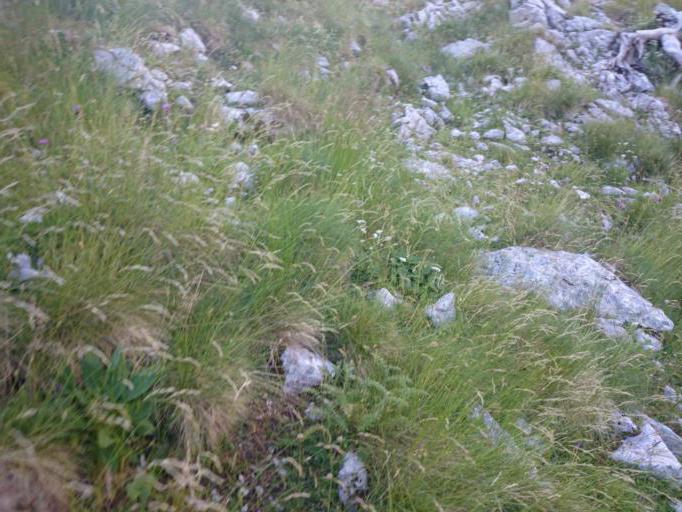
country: AL
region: Elbasan
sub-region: Rrethi i Gramshit
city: Kushove
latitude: 40.7174
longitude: 20.1461
